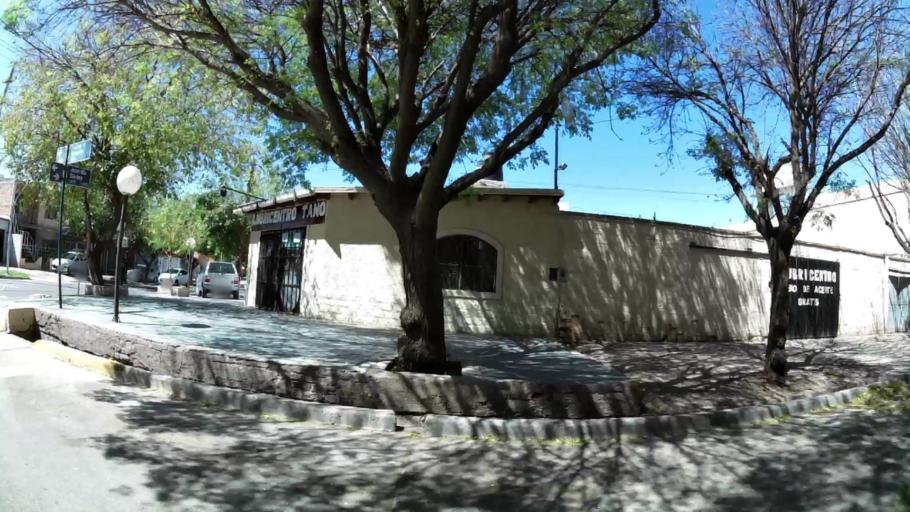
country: AR
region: Mendoza
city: Las Heras
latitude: -32.8605
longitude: -68.8471
